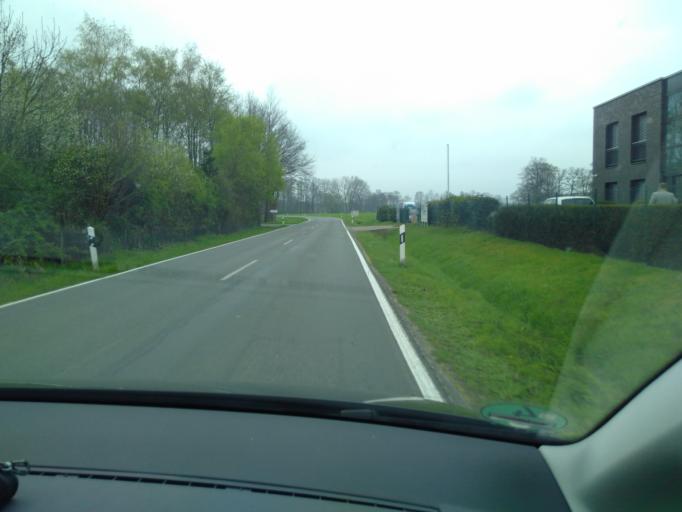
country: DE
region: North Rhine-Westphalia
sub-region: Regierungsbezirk Detmold
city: Verl
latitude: 51.8543
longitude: 8.5054
